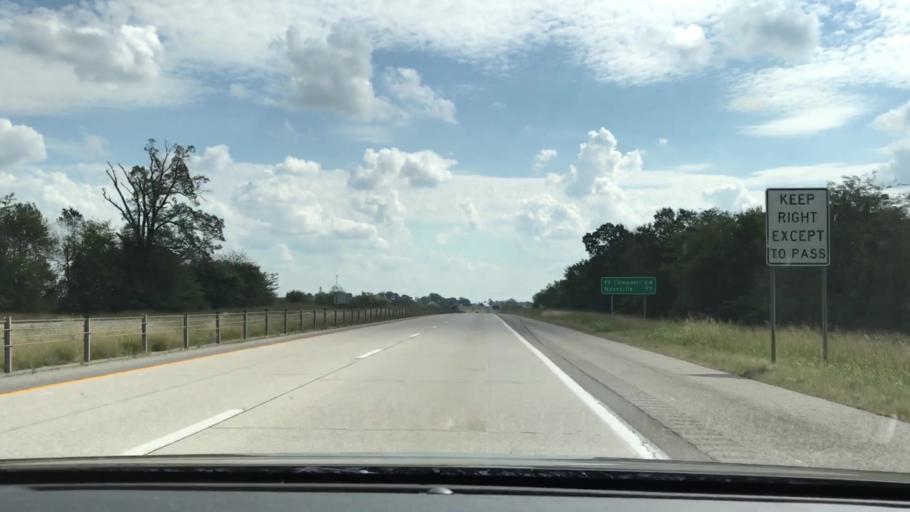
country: US
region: Kentucky
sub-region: Trigg County
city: Cadiz
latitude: 36.8747
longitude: -87.7232
